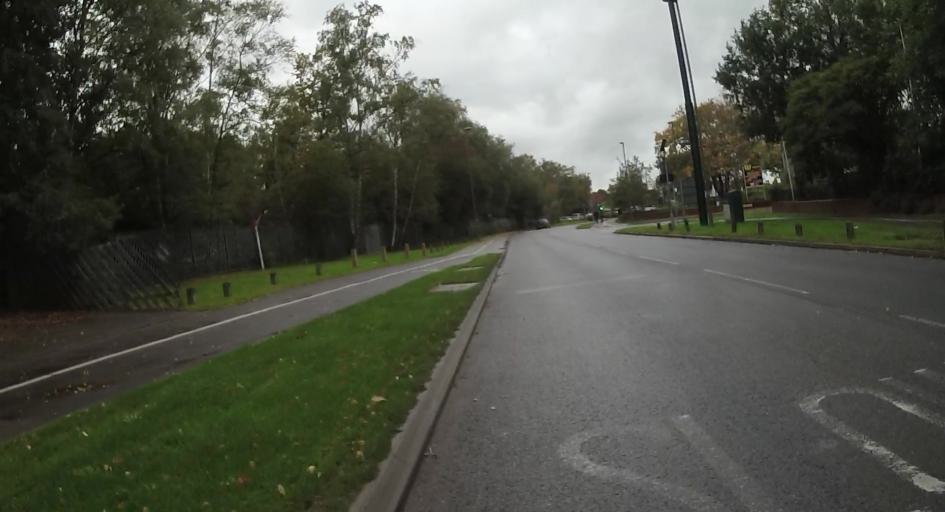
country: GB
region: England
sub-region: Surrey
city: Woking
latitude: 51.3274
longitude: -0.5363
